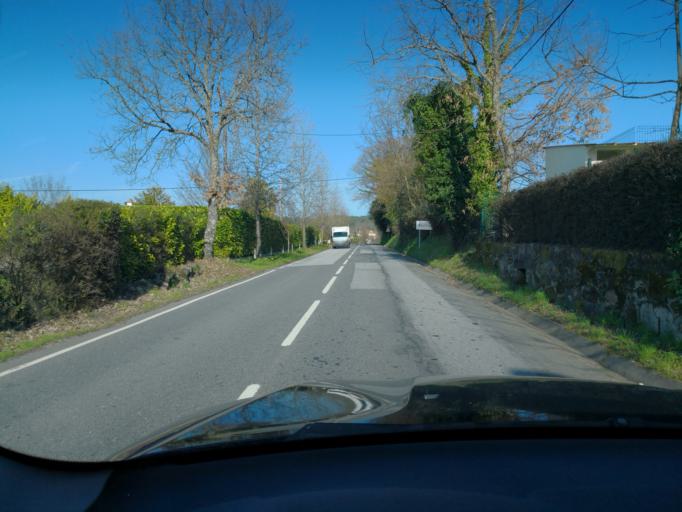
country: PT
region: Vila Real
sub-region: Vila Real
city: Vila Real
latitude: 41.3239
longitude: -7.6830
